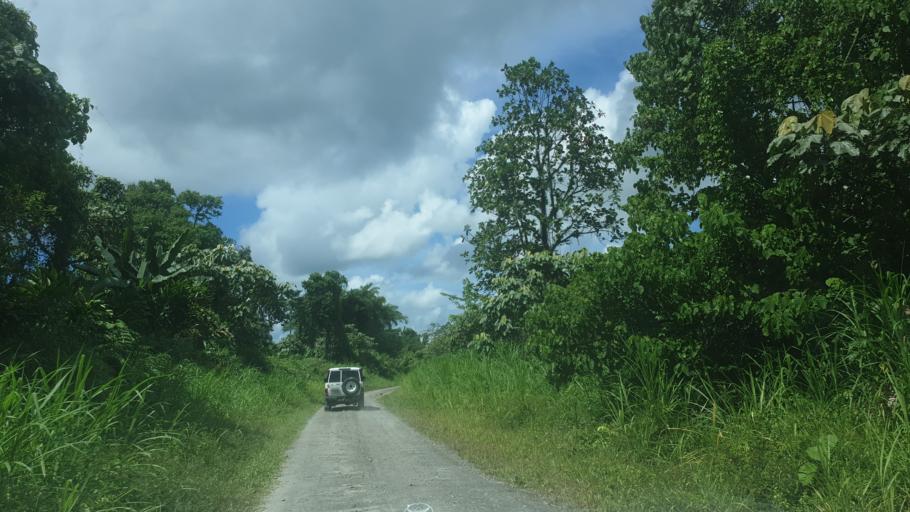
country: PG
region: Bougainville
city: Panguna
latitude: -6.7364
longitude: 155.5001
